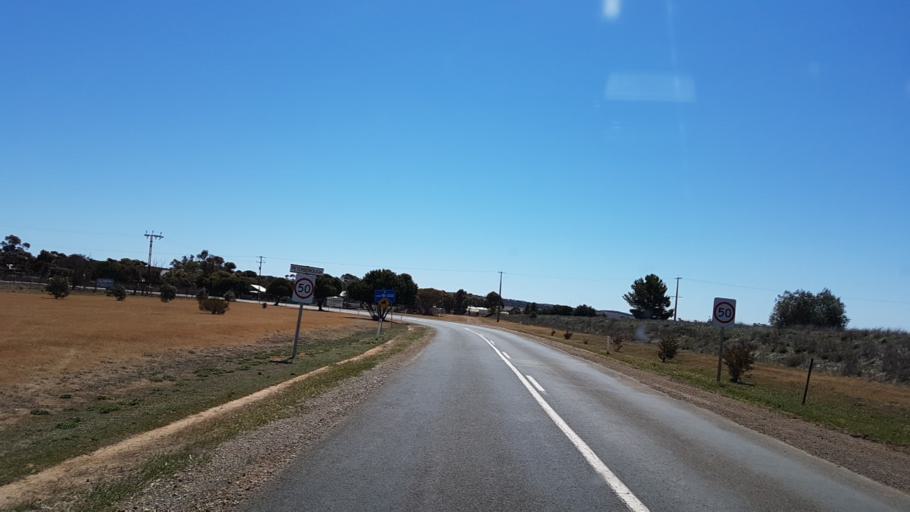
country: AU
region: South Australia
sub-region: Peterborough
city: Peterborough
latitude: -32.9787
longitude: 138.8456
